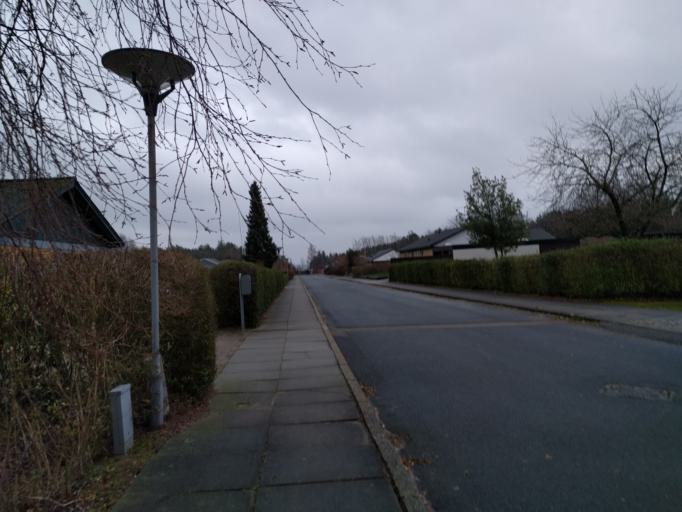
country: DK
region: Central Jutland
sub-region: Silkeborg Kommune
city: Silkeborg
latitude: 56.1904
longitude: 9.5331
